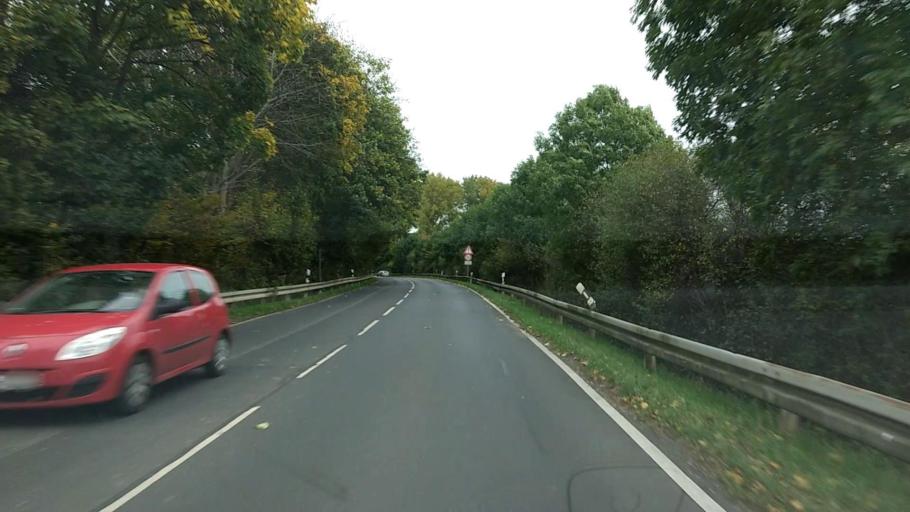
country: DE
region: North Rhine-Westphalia
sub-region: Regierungsbezirk Koln
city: Bergheim
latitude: 50.9242
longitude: 6.6801
